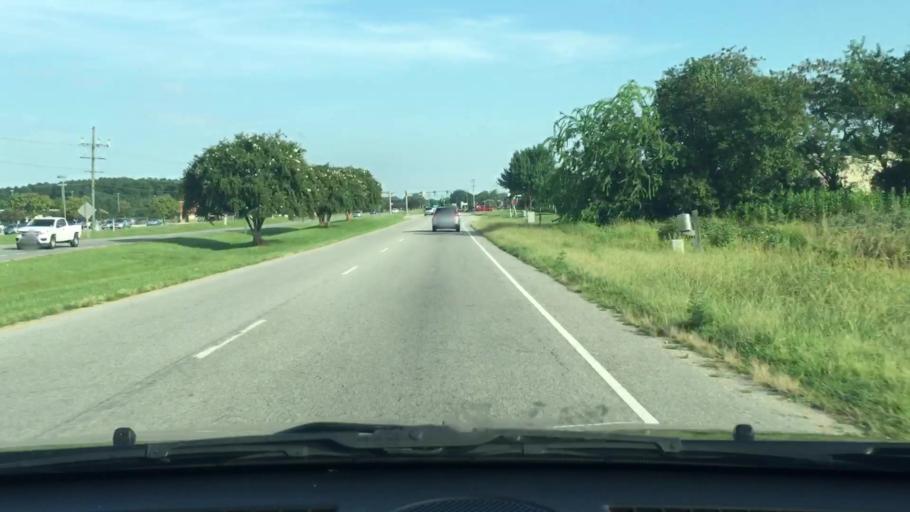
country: US
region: Virginia
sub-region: Isle of Wight County
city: Smithfield
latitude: 36.9548
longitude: -76.6011
